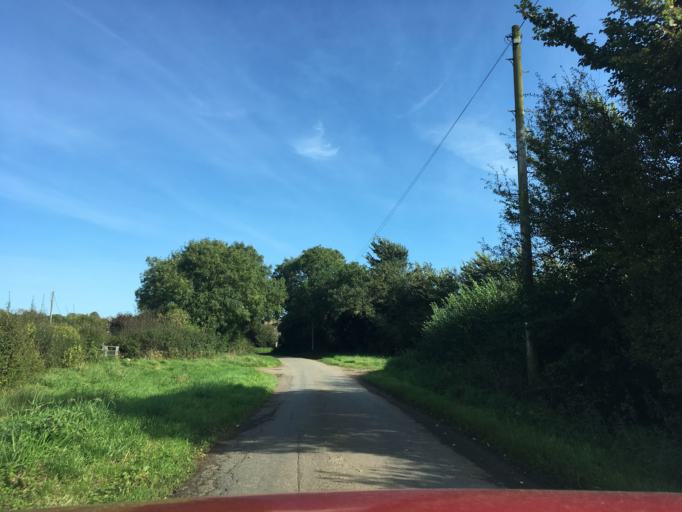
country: GB
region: England
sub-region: South Gloucestershire
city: Yate
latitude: 51.5655
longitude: -2.4155
